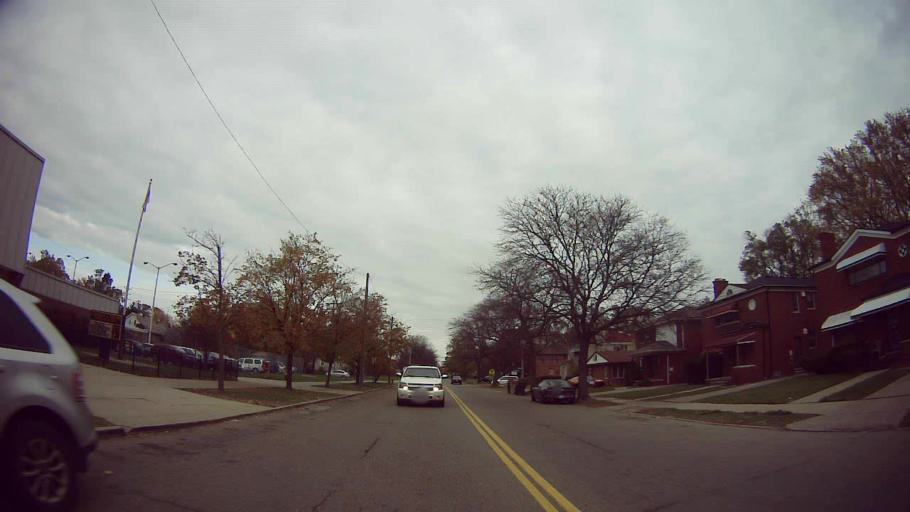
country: US
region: Michigan
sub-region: Oakland County
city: Oak Park
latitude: 42.4066
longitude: -83.1892
